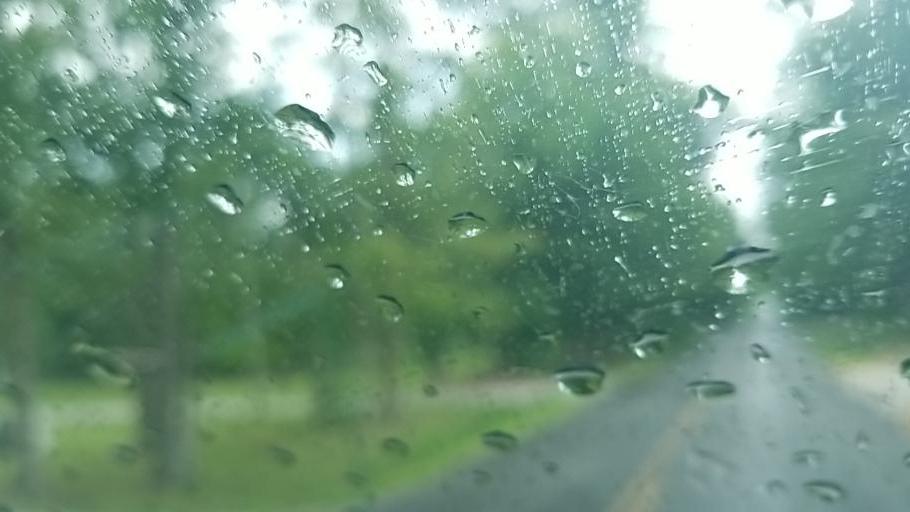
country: US
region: Ohio
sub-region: Lorain County
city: Lagrange
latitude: 41.1717
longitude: -82.0533
